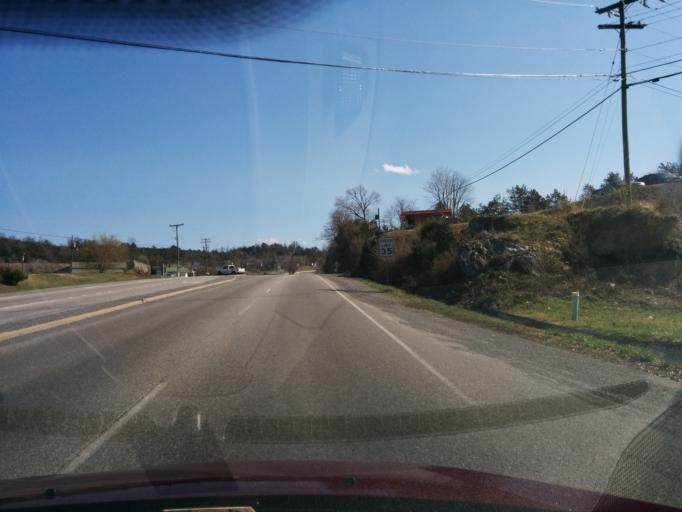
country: US
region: Virginia
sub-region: City of Lexington
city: Lexington
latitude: 37.7751
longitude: -79.4325
